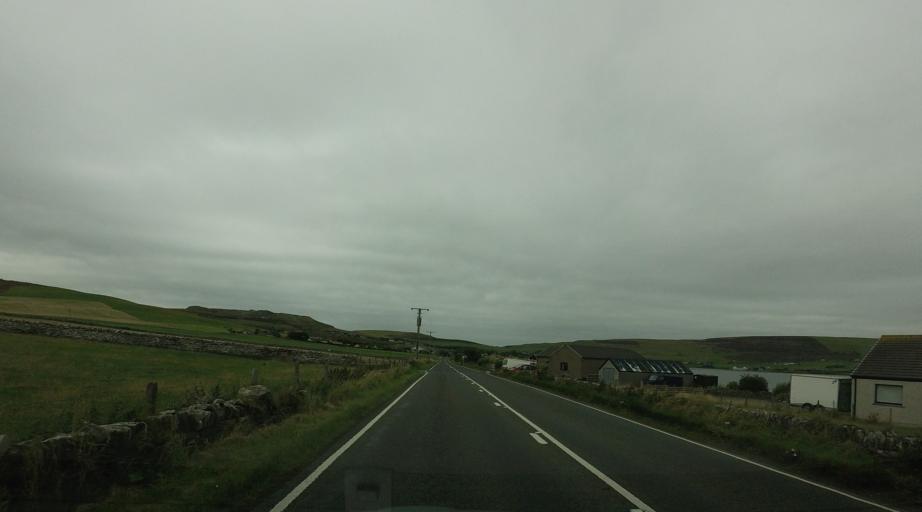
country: GB
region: Scotland
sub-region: Orkney Islands
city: Orkney
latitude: 59.0007
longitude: -3.0946
